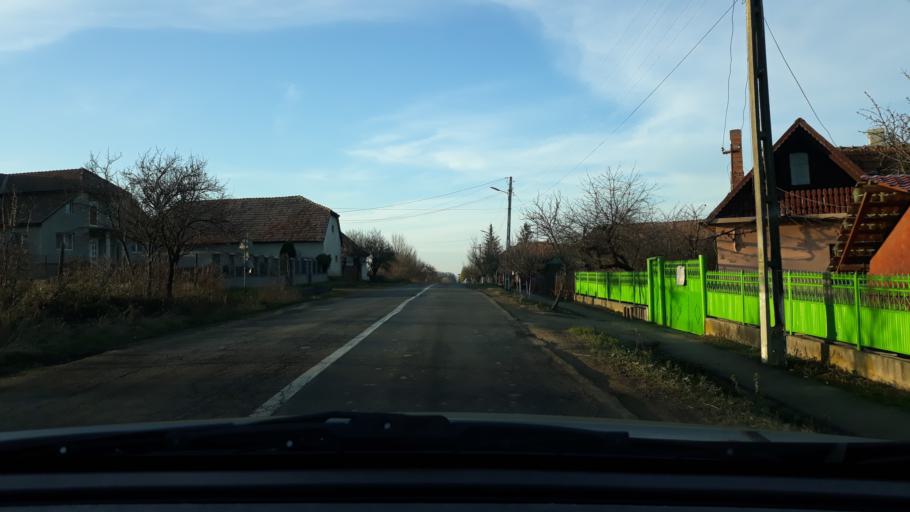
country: RO
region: Bihor
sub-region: Comuna Balc
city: Balc
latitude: 47.2730
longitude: 22.4898
